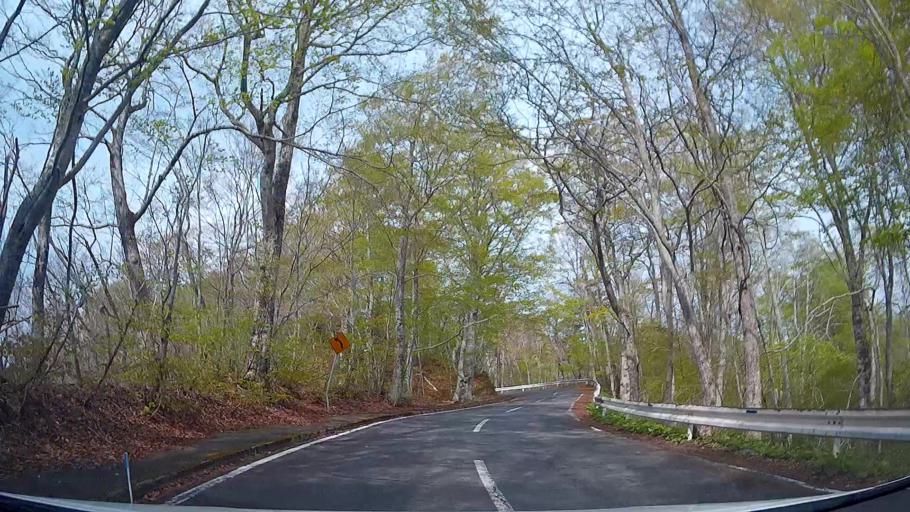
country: JP
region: Akita
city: Hanawa
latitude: 40.4383
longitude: 140.9168
